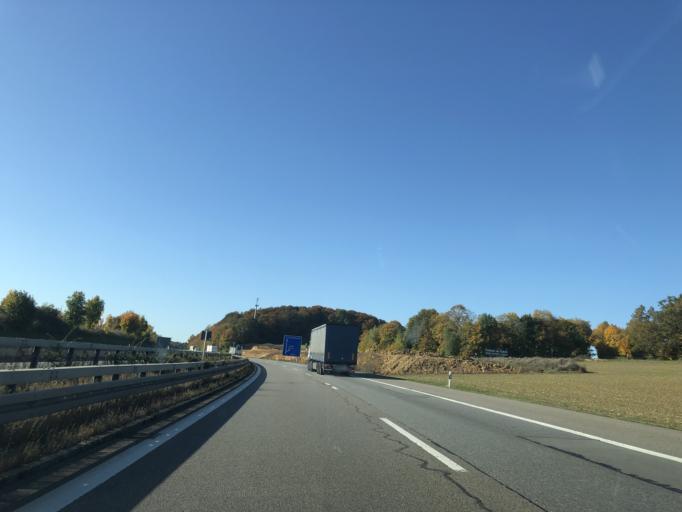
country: DE
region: Bavaria
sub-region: Upper Palatinate
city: Brunn
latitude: 49.0841
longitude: 11.8998
